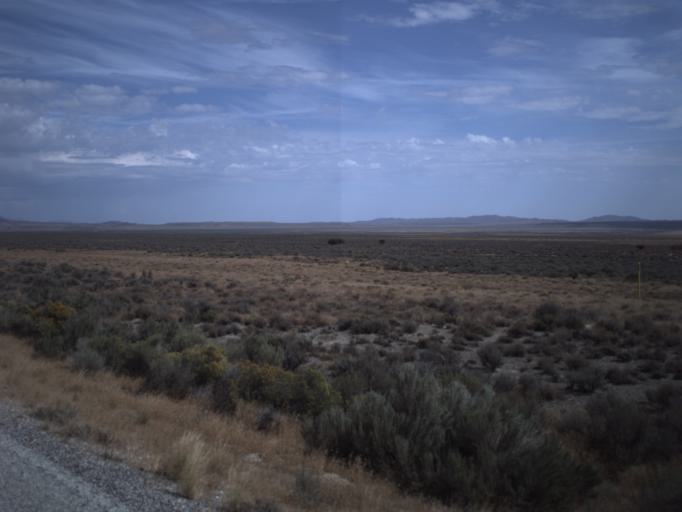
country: US
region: Utah
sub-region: Tooele County
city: Wendover
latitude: 41.5204
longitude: -113.5974
